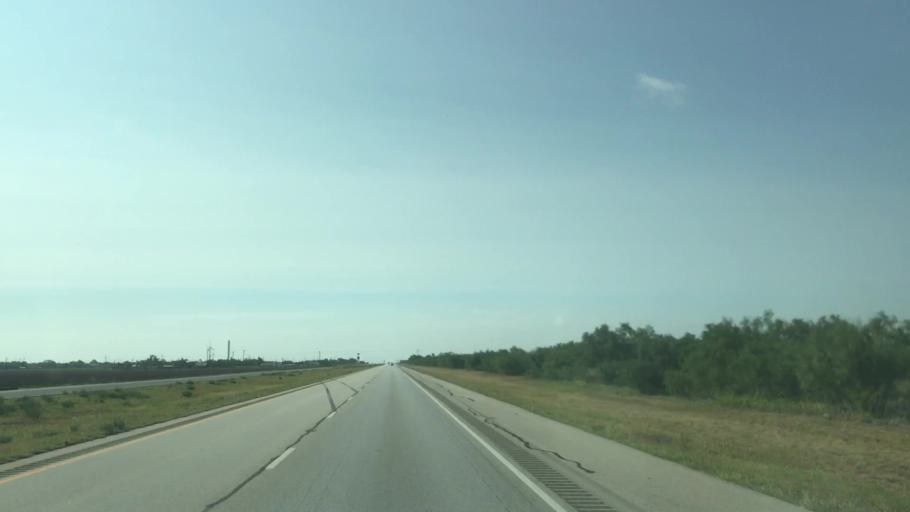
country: US
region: Texas
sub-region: Scurry County
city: Snyder
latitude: 32.6456
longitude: -100.7725
